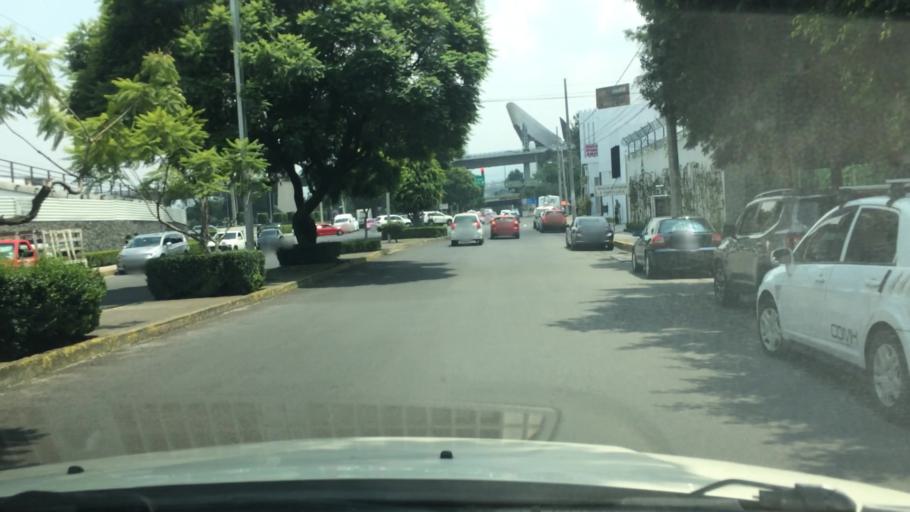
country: MX
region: Mexico City
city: Tlalpan
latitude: 19.3046
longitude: -99.1933
